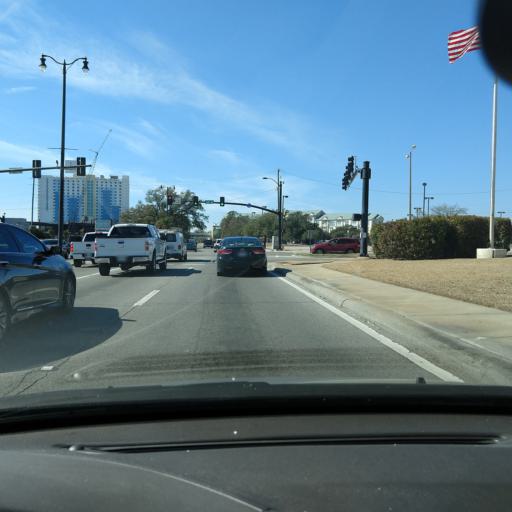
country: US
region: Mississippi
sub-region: Harrison County
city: Gulfport
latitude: 30.3645
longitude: -89.0971
